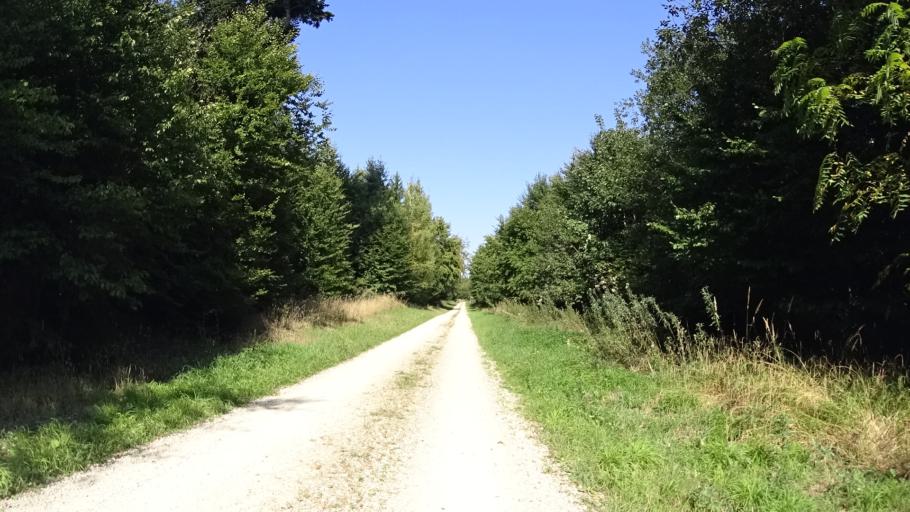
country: DE
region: Bavaria
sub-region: Upper Bavaria
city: Walting
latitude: 48.9588
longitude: 11.3565
